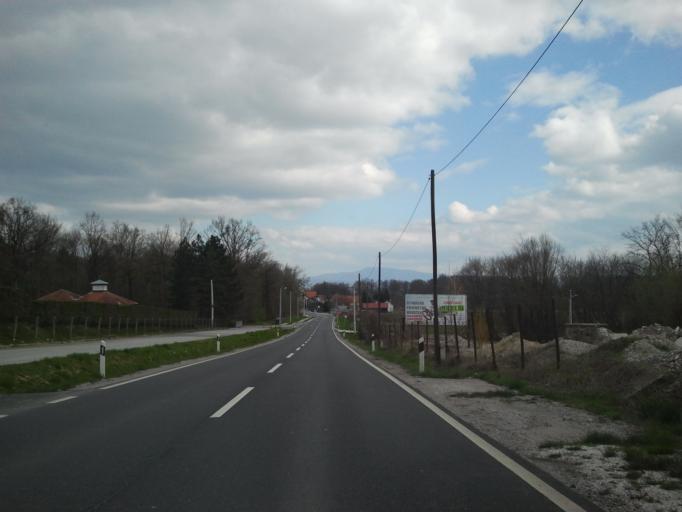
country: HR
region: Zagrebacka
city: Kerestinec
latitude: 45.7306
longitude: 15.7870
